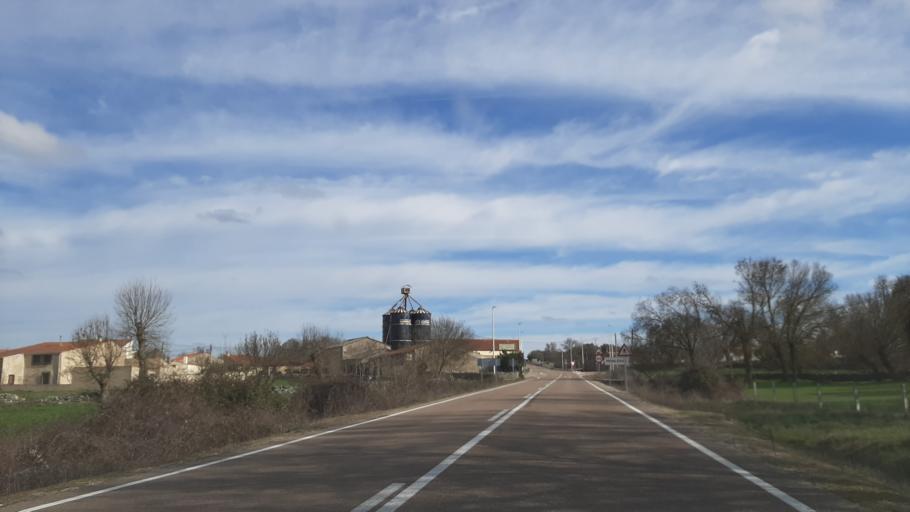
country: ES
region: Castille and Leon
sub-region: Provincia de Salamanca
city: Monleras
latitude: 41.1839
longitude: -6.2279
